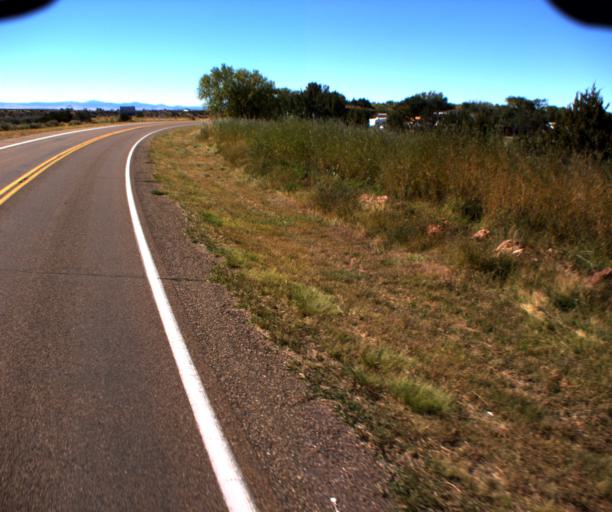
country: US
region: Arizona
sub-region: Apache County
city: Saint Johns
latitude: 34.4926
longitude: -109.3708
